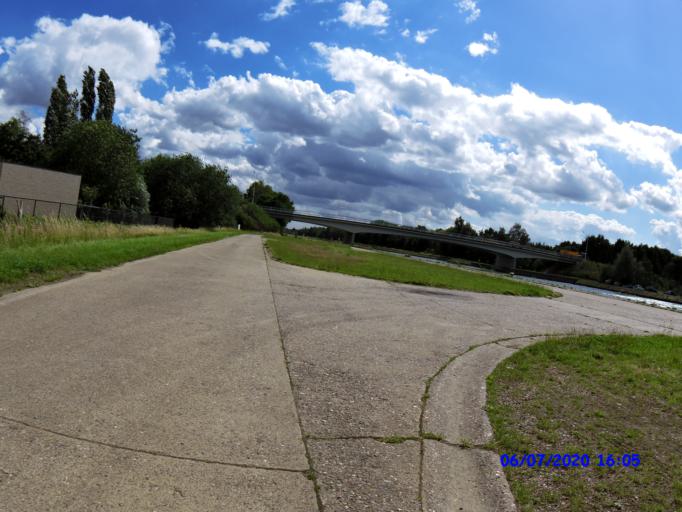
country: BE
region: Flanders
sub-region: Provincie Antwerpen
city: Balen
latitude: 51.1397
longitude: 5.1450
